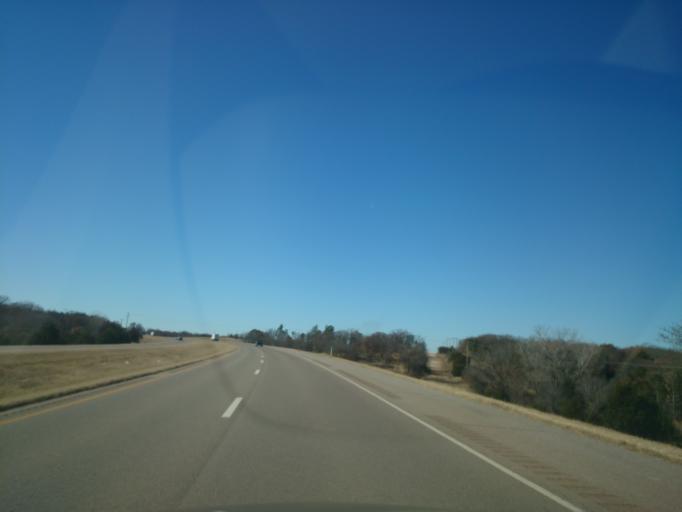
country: US
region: Oklahoma
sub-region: Payne County
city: Stillwater
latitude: 36.1160
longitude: -97.1870
